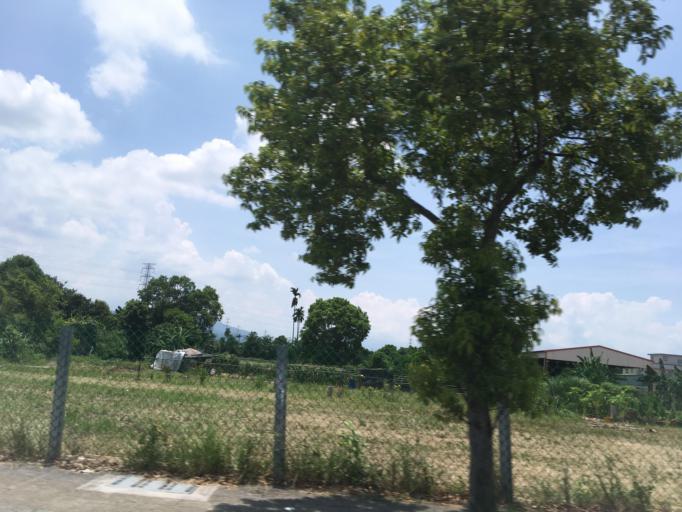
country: TW
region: Taiwan
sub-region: Yilan
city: Yilan
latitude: 24.6618
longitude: 121.7609
